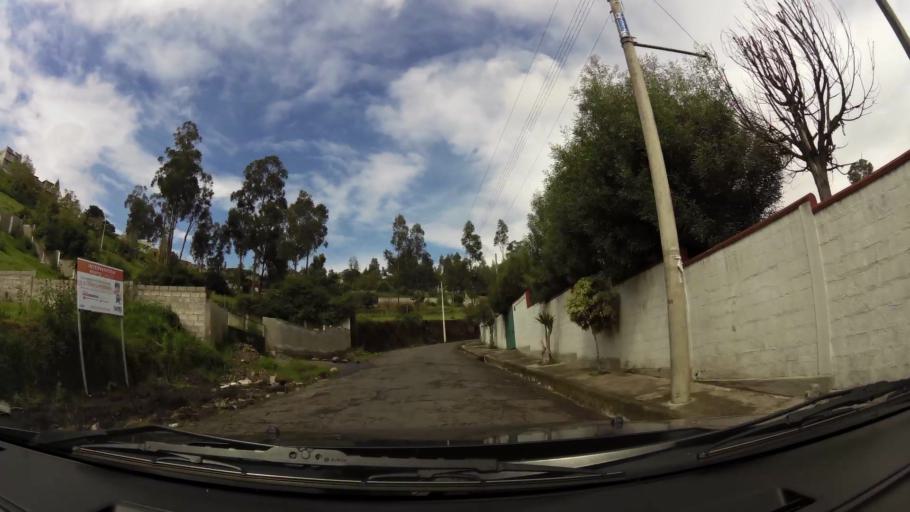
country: EC
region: Pichincha
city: Sangolqui
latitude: -0.3043
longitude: -78.4286
